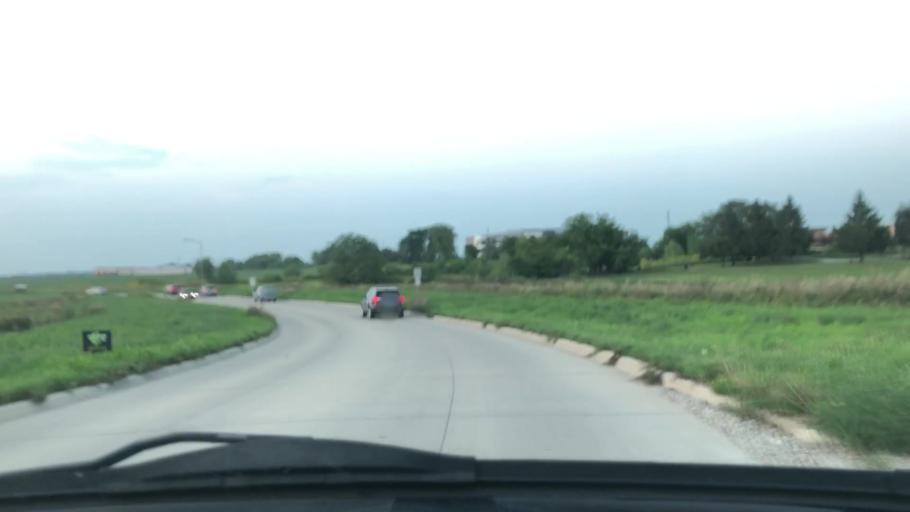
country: US
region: Iowa
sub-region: Johnson County
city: North Liberty
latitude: 41.7146
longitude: -91.6051
